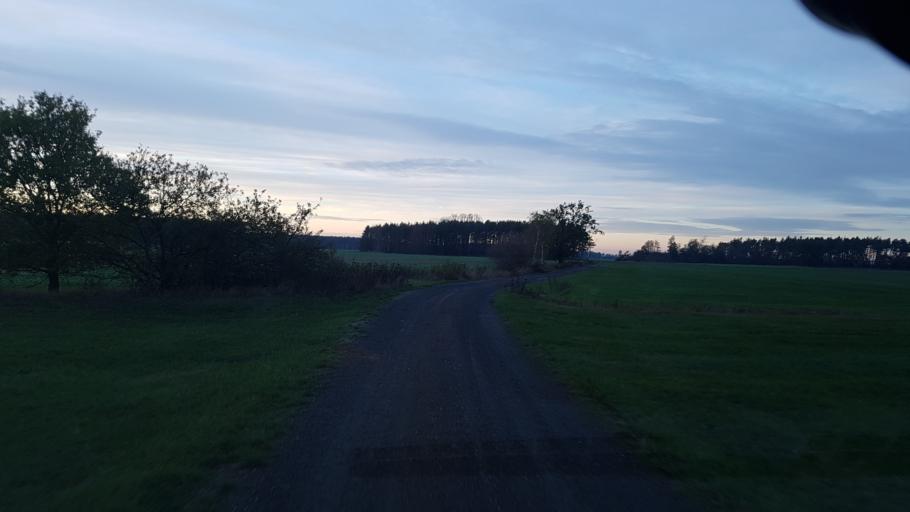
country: DE
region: Brandenburg
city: Falkenberg
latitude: 51.5325
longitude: 13.2778
